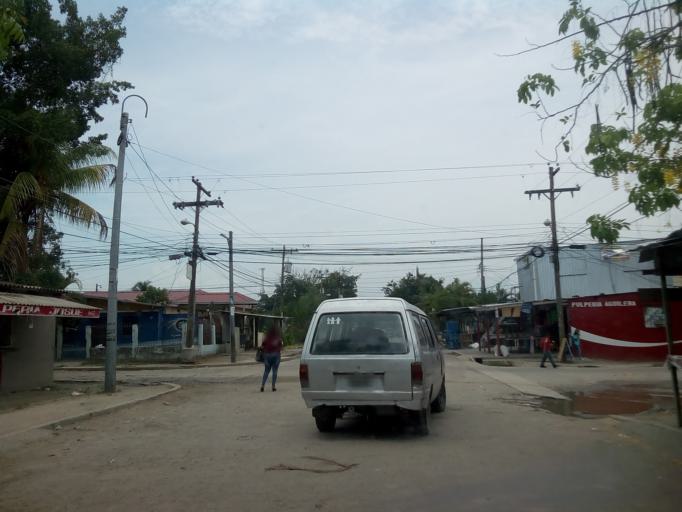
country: HN
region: Cortes
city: La Lima
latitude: 15.4603
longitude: -87.9480
